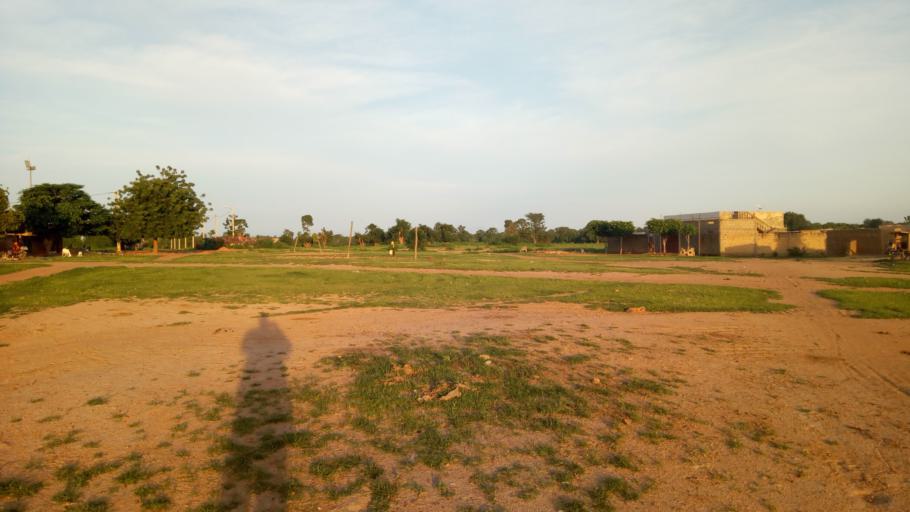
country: ML
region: Sikasso
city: Koutiala
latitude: 12.4009
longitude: -5.4456
